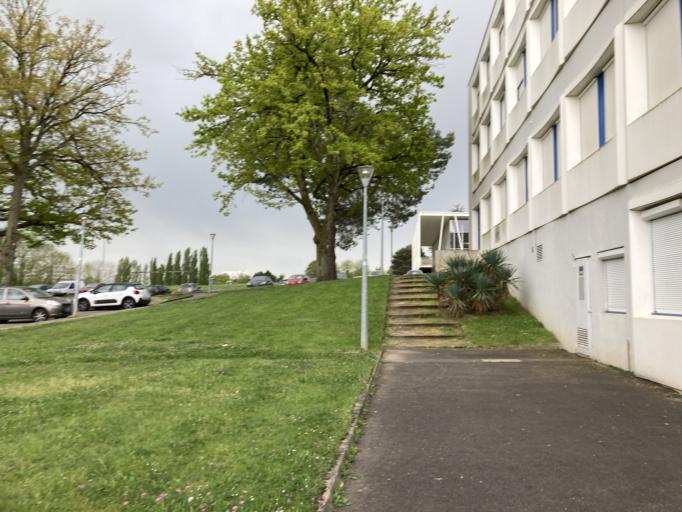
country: FR
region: Limousin
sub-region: Departement de la Haute-Vienne
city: Isle
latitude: 45.8169
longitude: 1.2302
